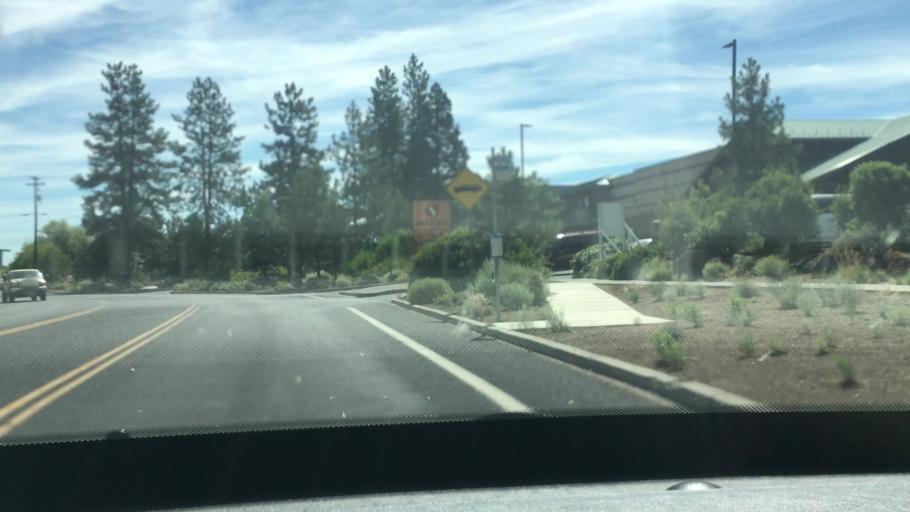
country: US
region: Oregon
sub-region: Deschutes County
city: Bend
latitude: 44.0478
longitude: -121.3305
